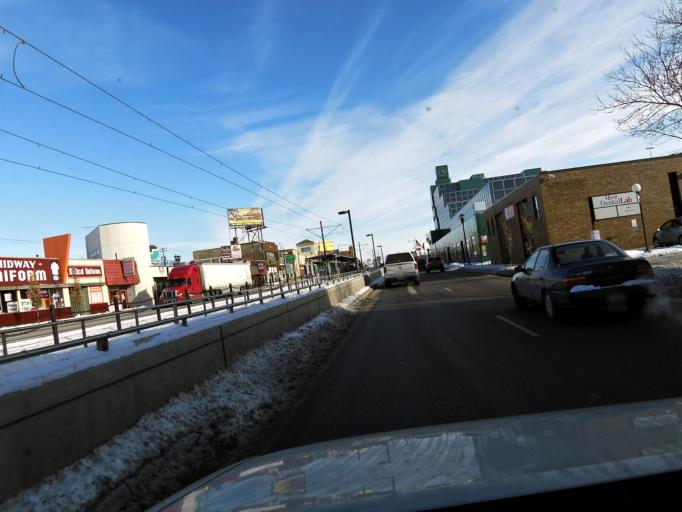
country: US
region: Minnesota
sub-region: Ramsey County
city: Falcon Heights
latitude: 44.9555
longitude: -93.1694
